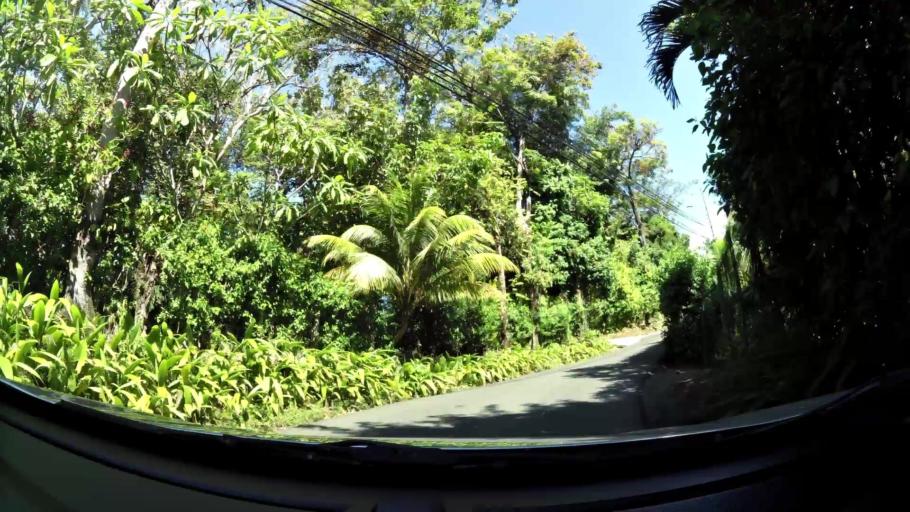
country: CR
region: Puntarenas
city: Quepos
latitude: 9.4045
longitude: -84.1597
